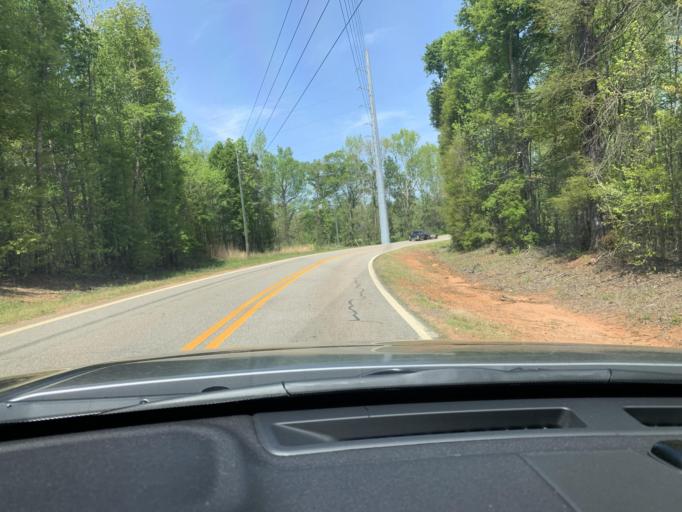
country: US
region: Georgia
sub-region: Oconee County
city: Bogart
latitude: 33.9108
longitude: -83.5608
